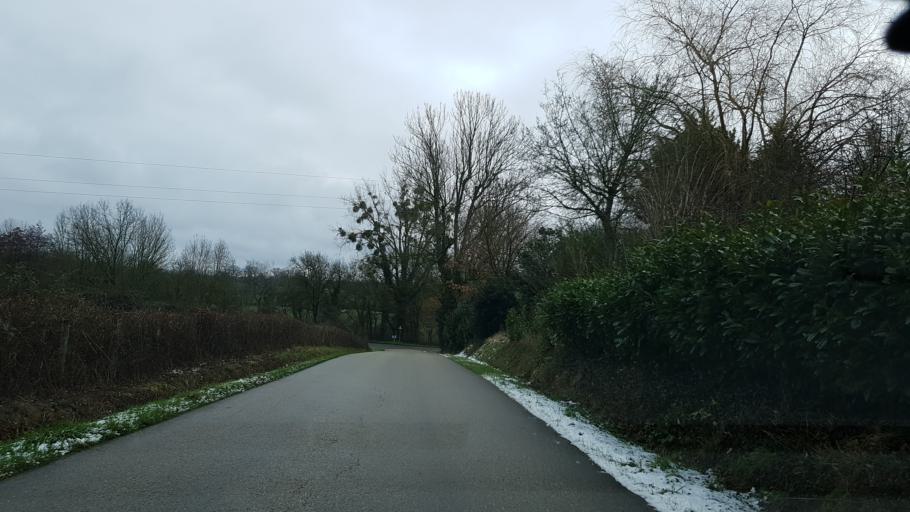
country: FR
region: Rhone-Alpes
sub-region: Departement de l'Ain
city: Saint-Denis-les-Bourg
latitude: 46.1851
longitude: 5.1760
